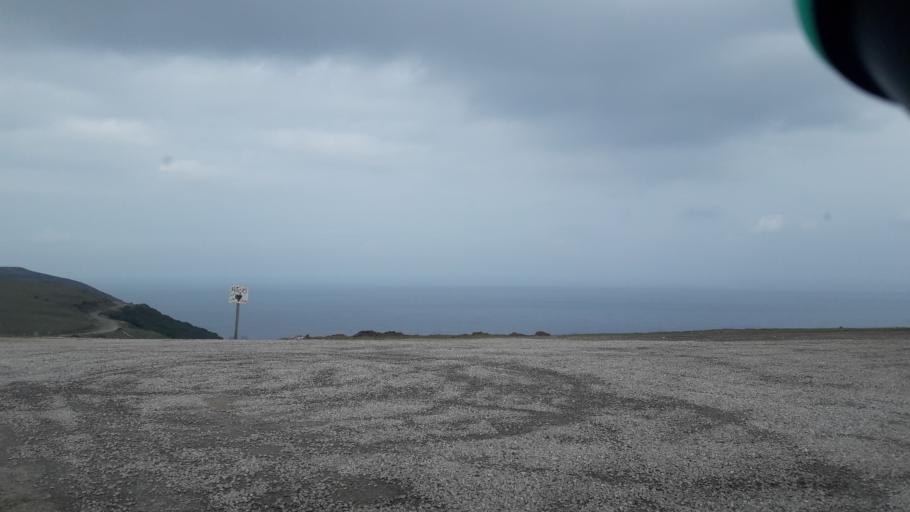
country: TR
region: Sinop
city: Sinop
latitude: 42.0198
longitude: 35.2043
